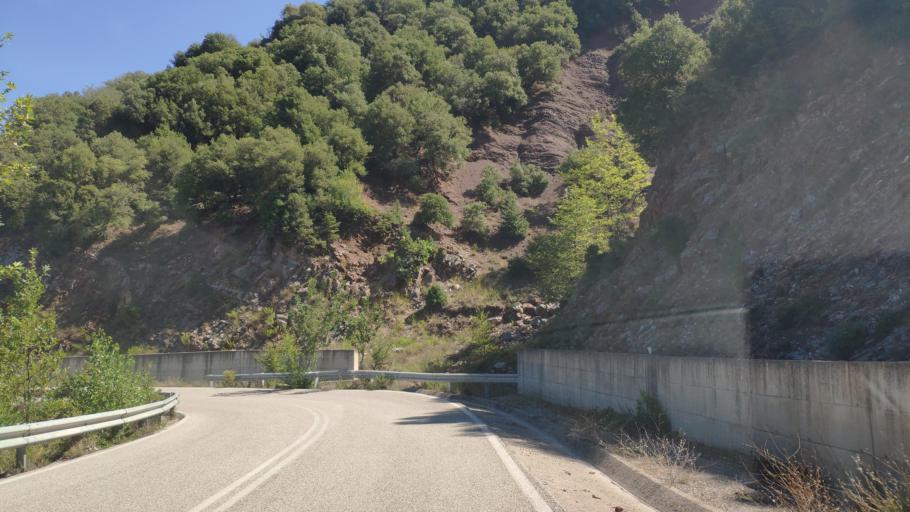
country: GR
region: Central Greece
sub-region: Nomos Evrytanias
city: Kerasochori
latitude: 39.0092
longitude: 21.5954
